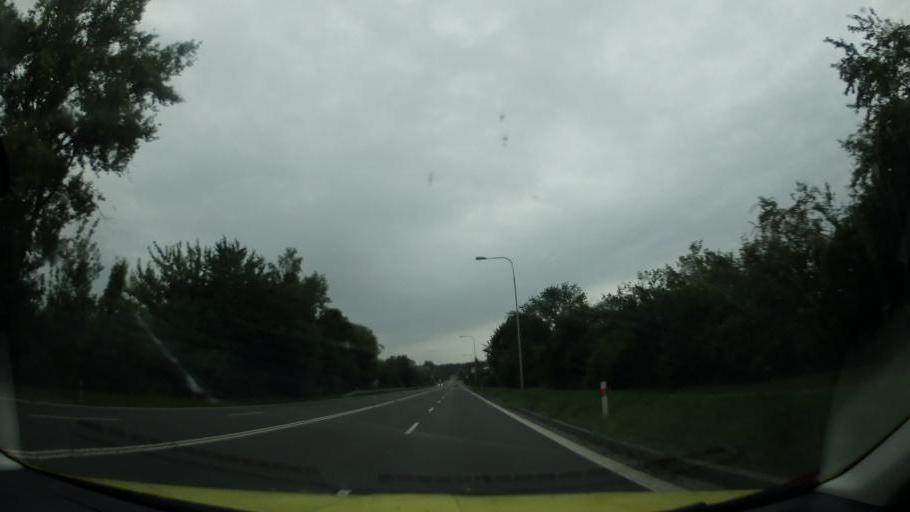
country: CZ
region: Olomoucky
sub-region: Okres Prerov
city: Hranice
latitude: 49.5598
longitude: 17.7538
